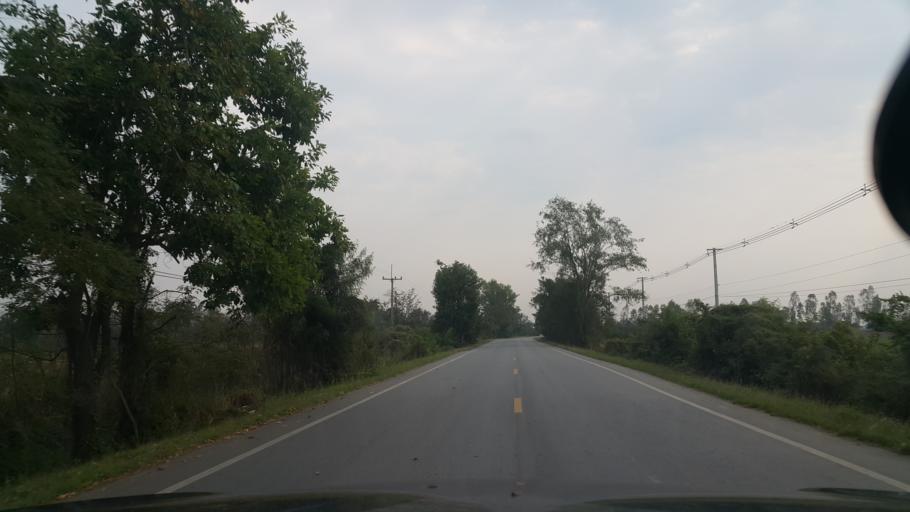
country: TH
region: Sukhothai
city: Si Samrong
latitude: 17.1710
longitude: 99.7232
